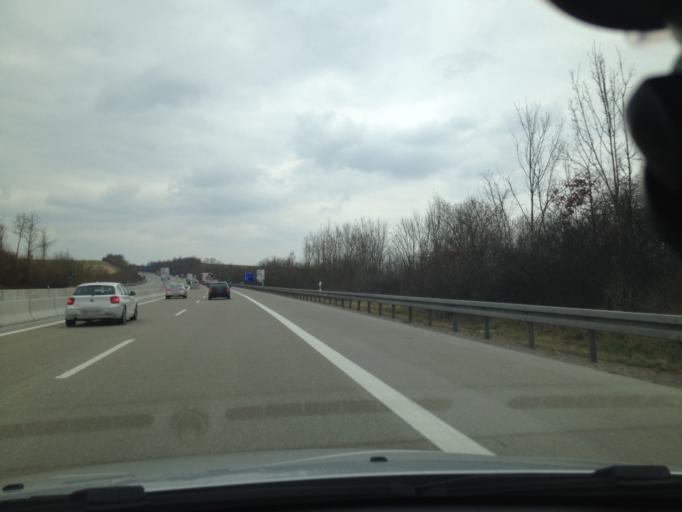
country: DE
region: Bavaria
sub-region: Regierungsbezirk Unterfranken
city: Obernbreit
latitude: 49.6435
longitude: 10.1654
